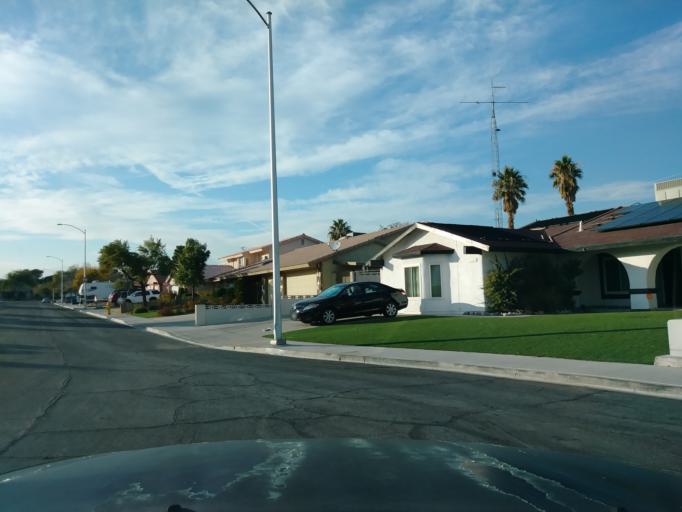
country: US
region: Nevada
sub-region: Clark County
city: Spring Valley
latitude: 36.1725
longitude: -115.2390
